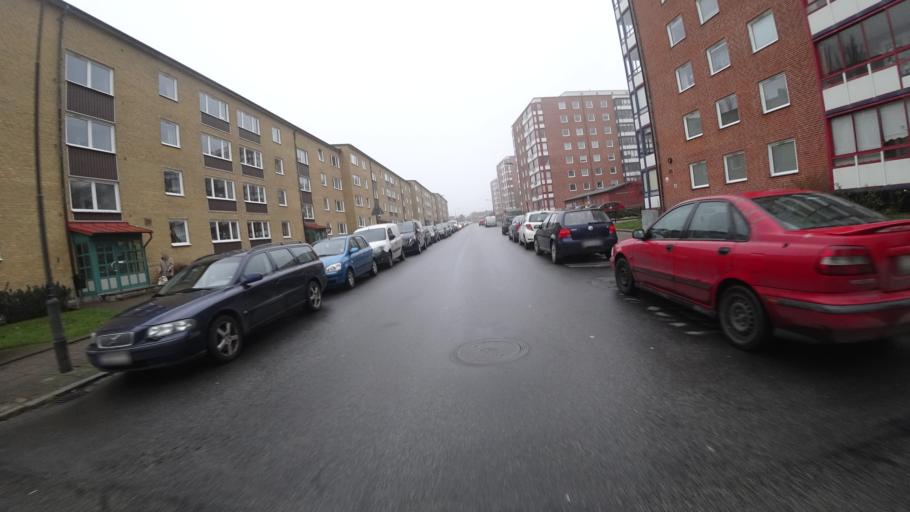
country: SE
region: Skane
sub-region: Malmo
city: Malmoe
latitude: 55.5682
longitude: 13.0082
